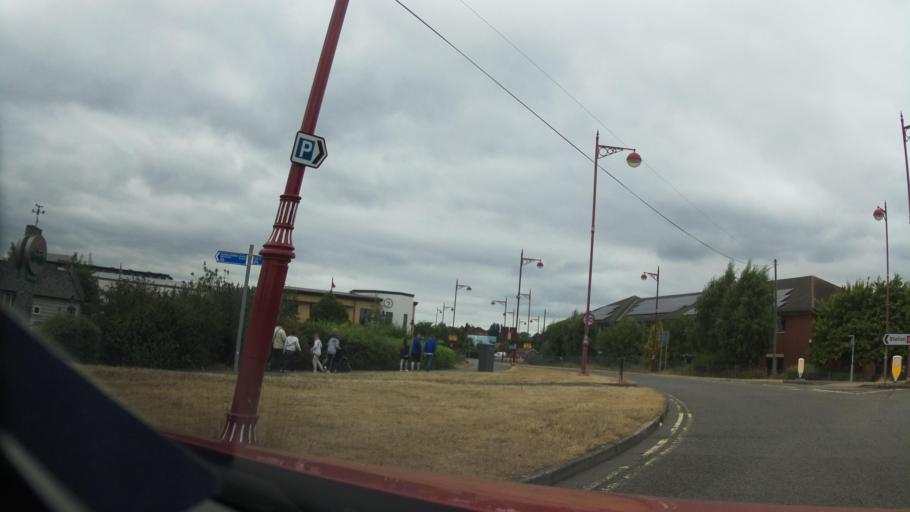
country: GB
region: England
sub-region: Derby
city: Derby
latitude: 52.9156
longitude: -1.4572
